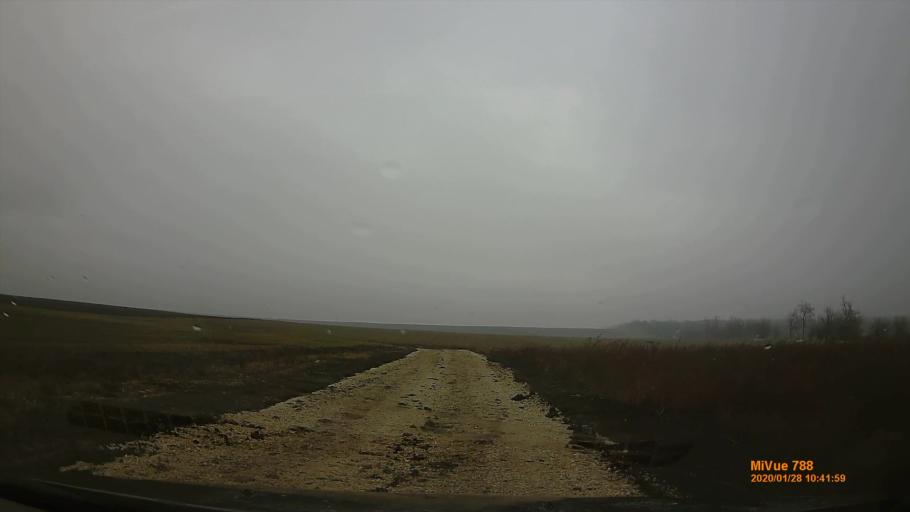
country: HU
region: Pest
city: Monor
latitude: 47.3612
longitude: 19.4876
